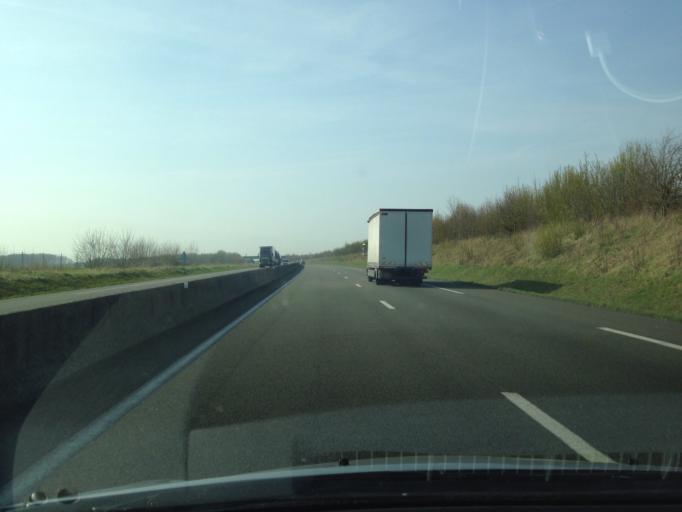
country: FR
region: Picardie
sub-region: Departement de la Somme
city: Sailly-Flibeaucourt
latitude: 50.1537
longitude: 1.7921
